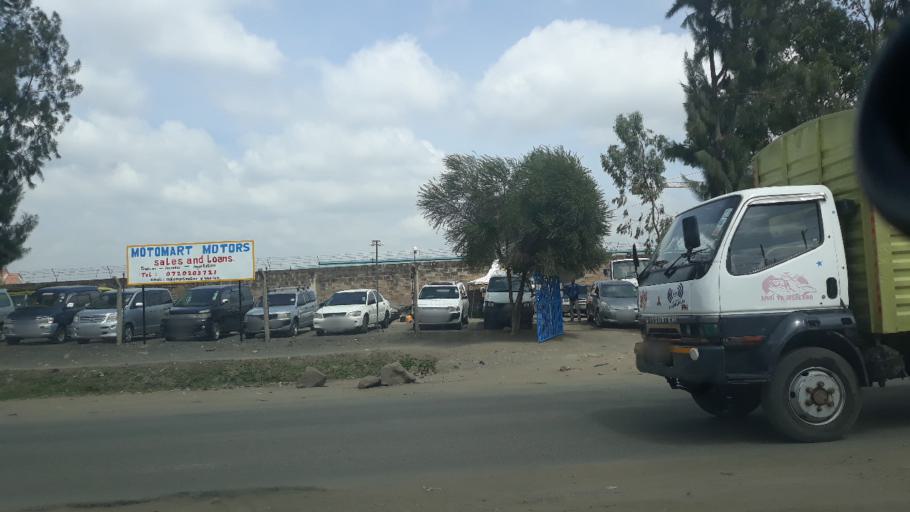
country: KE
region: Nairobi Area
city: Pumwani
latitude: -1.2748
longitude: 36.8933
